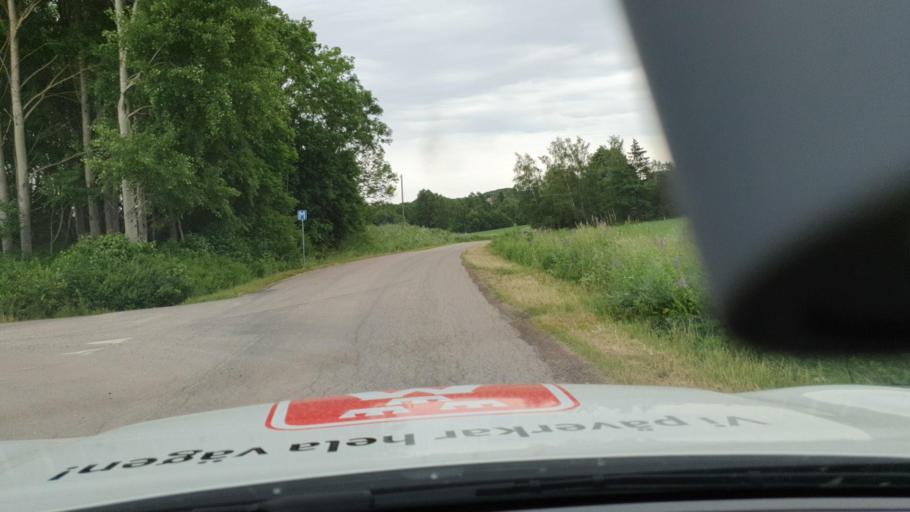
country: SE
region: Vaestra Goetaland
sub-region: Skovde Kommun
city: Skoevde
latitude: 58.3706
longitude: 13.8749
